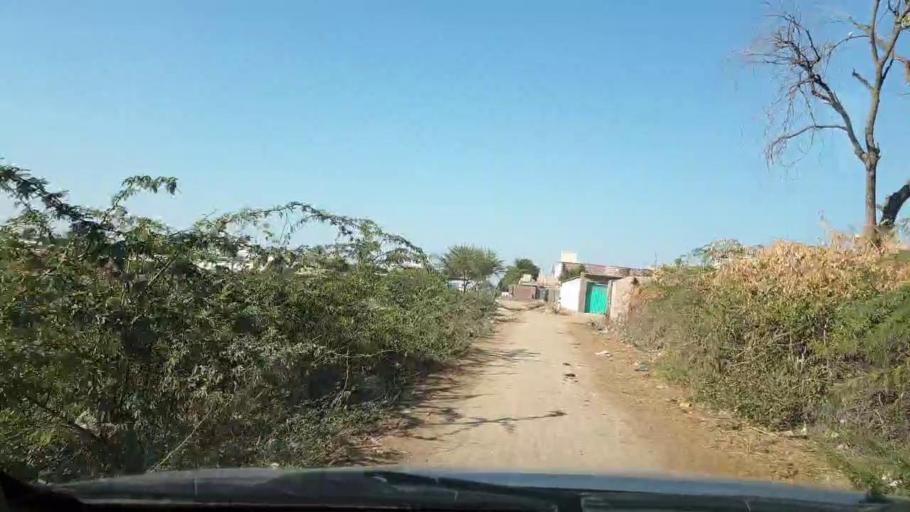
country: PK
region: Sindh
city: Berani
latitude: 25.8189
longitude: 68.9421
